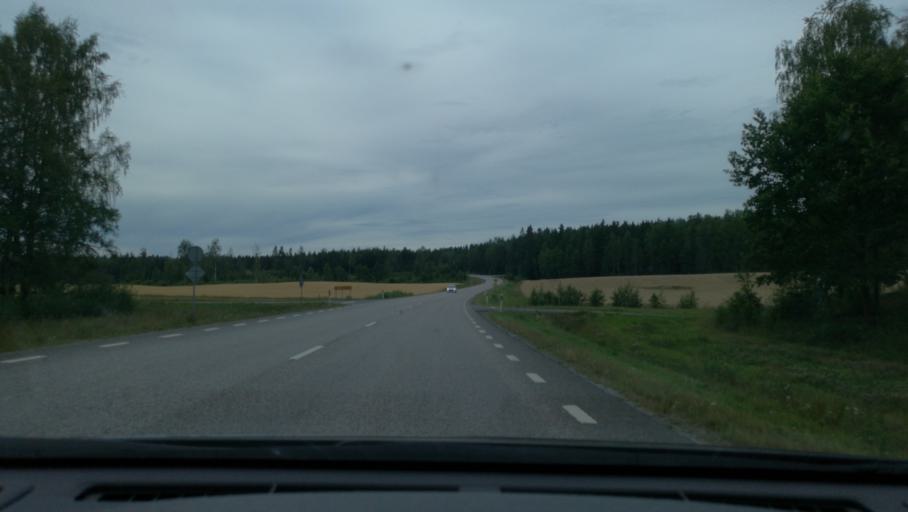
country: SE
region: Soedermanland
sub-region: Katrineholms Kommun
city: Katrineholm
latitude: 59.0899
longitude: 16.1948
